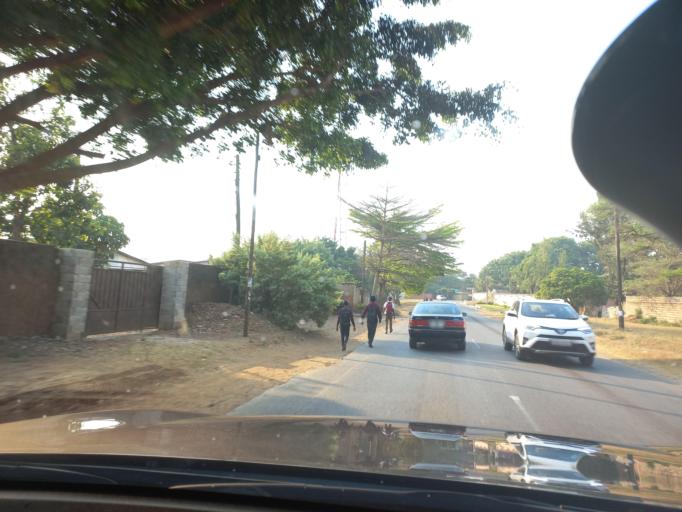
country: ZM
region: Lusaka
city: Lusaka
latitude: -15.4153
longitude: 28.3550
